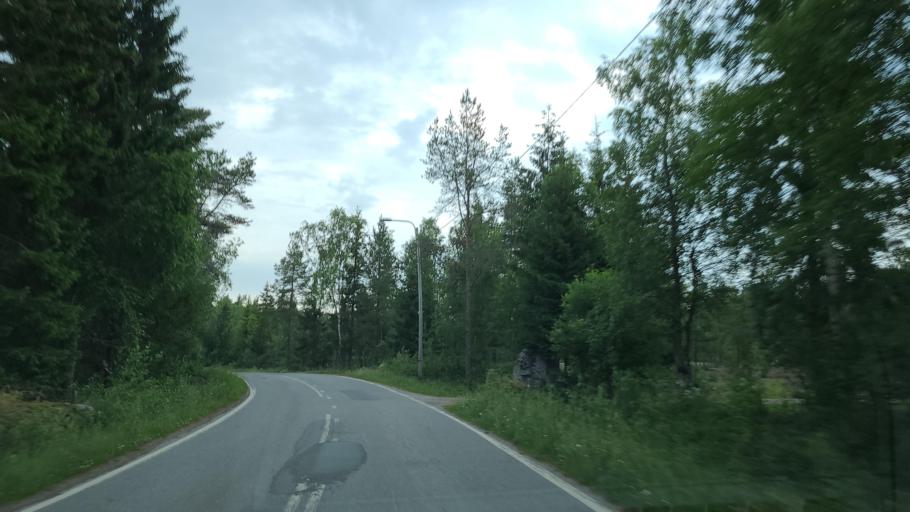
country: FI
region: Ostrobothnia
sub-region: Vaasa
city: Replot
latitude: 63.1742
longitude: 21.2775
